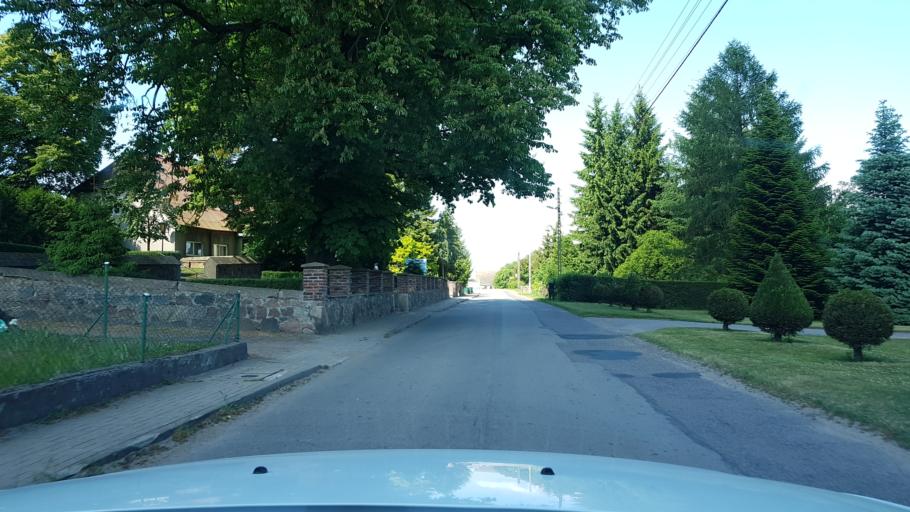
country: PL
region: West Pomeranian Voivodeship
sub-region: Powiat gryfinski
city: Banie
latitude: 53.0401
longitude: 14.6249
